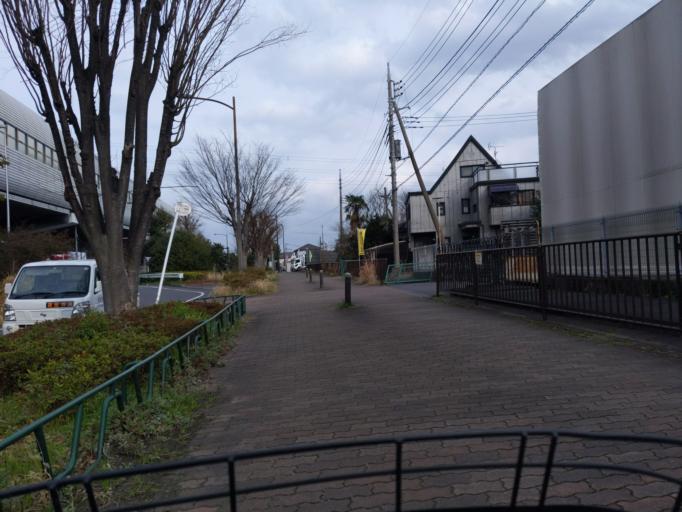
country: JP
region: Saitama
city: Soka
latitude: 35.8477
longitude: 139.7849
